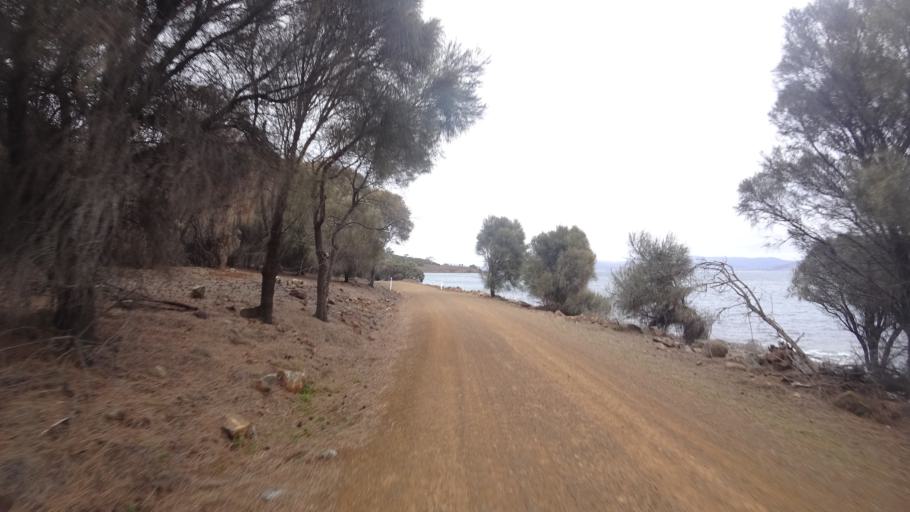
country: AU
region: Tasmania
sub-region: Sorell
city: Sorell
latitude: -42.6155
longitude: 148.0370
